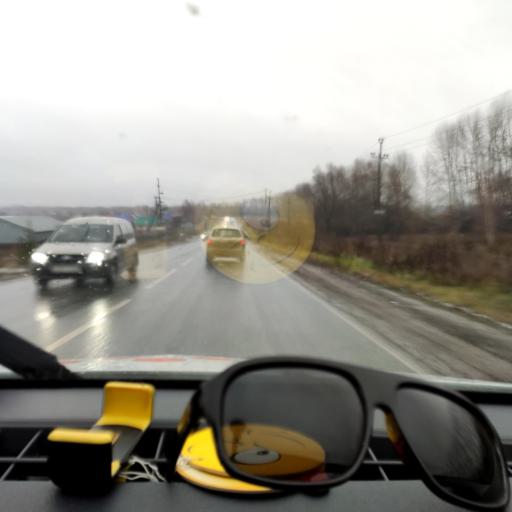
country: RU
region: Bashkortostan
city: Iglino
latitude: 54.7932
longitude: 56.2773
